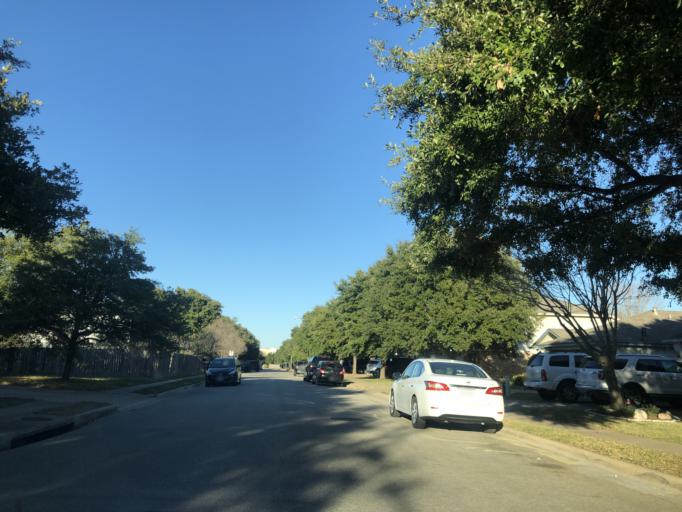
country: US
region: Texas
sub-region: Travis County
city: Windemere
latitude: 30.4788
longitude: -97.6559
